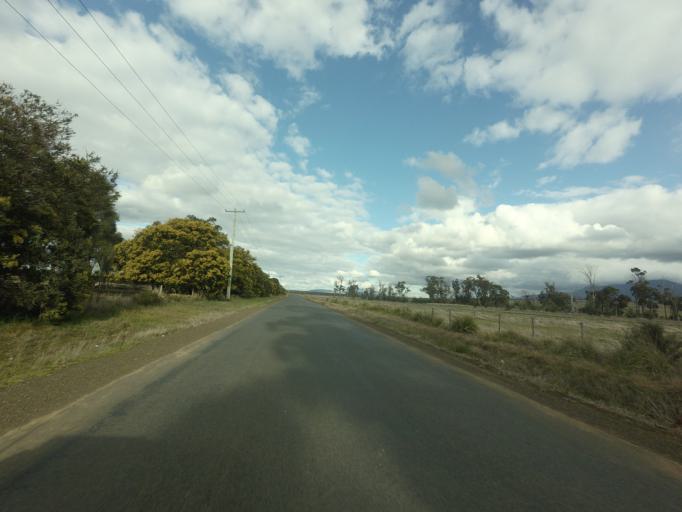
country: AU
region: Tasmania
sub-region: Northern Midlands
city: Longford
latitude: -41.8150
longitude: 147.1933
